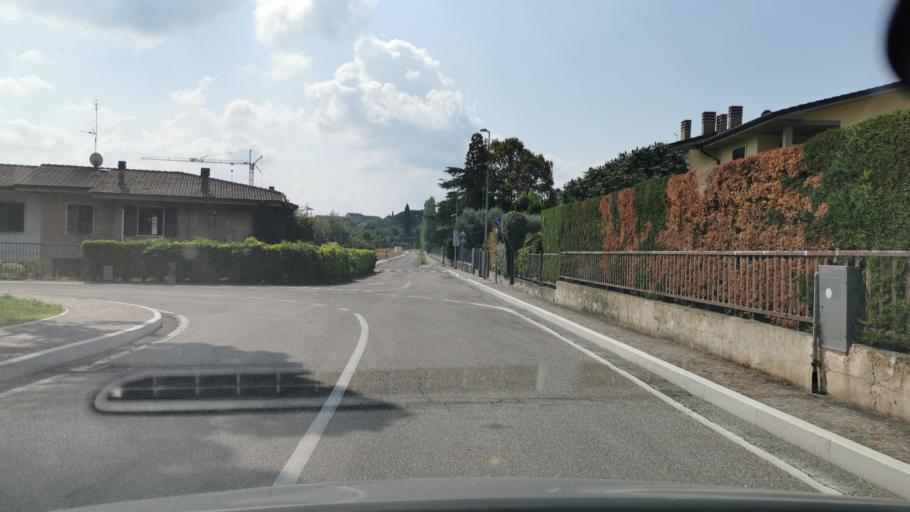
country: IT
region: Veneto
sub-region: Provincia di Verona
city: Cavajon Veronese
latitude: 45.5518
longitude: 10.7729
